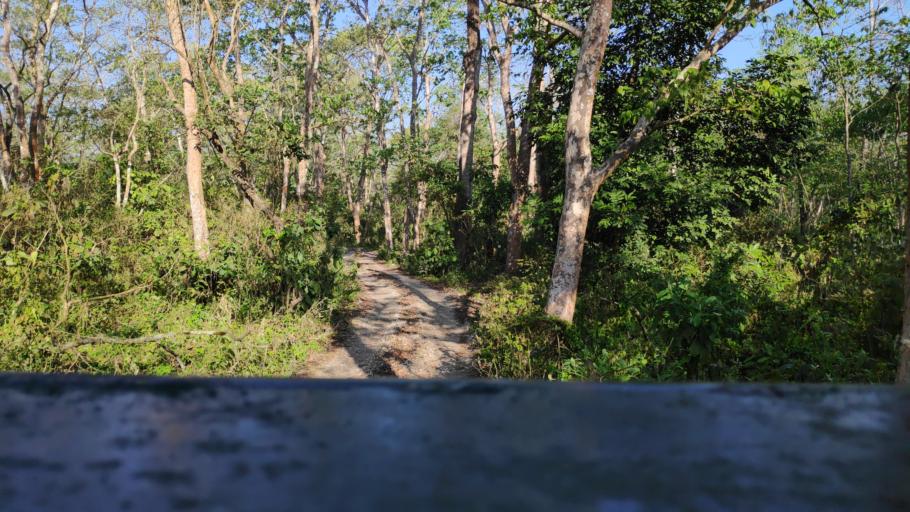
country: NP
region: Central Region
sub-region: Narayani Zone
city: Bharatpur
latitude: 27.5586
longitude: 84.5514
